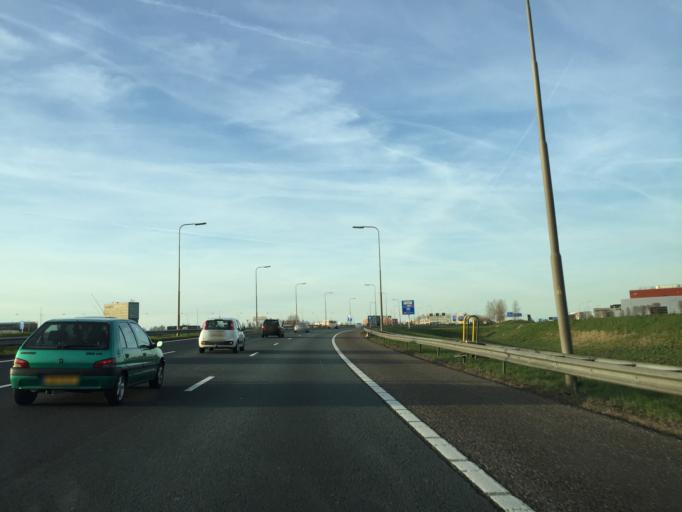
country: NL
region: South Holland
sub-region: Gemeente Den Haag
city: Ypenburg
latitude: 52.0417
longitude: 4.3525
